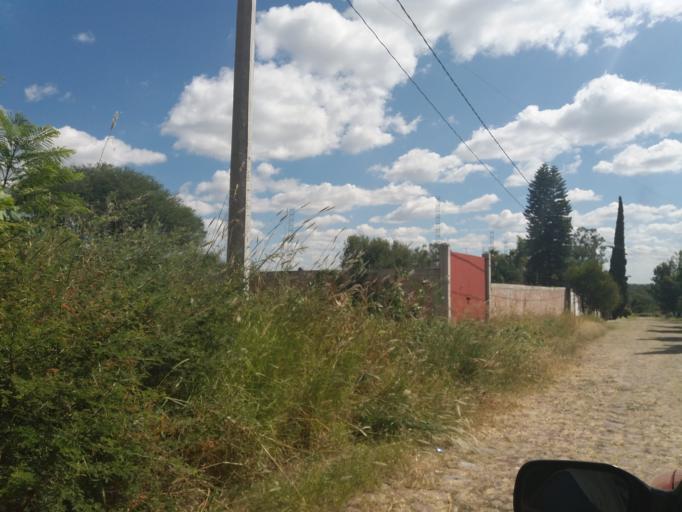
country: MX
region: Aguascalientes
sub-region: Aguascalientes
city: San Sebastian [Fraccionamiento]
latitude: 21.7871
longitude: -102.2767
